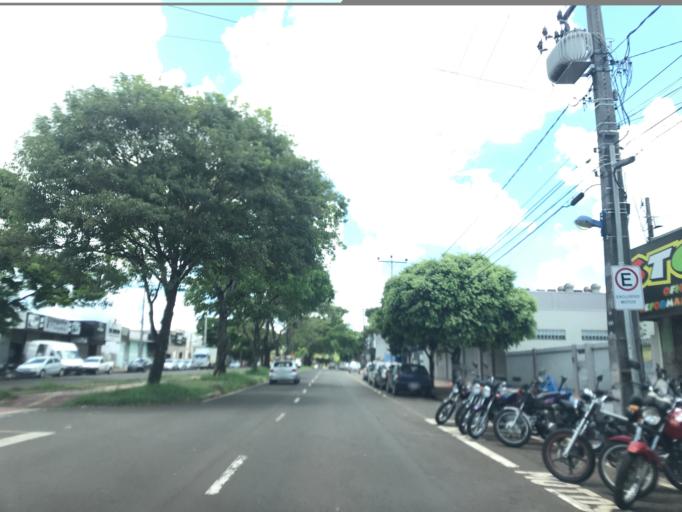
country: BR
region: Parana
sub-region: Maringa
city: Maringa
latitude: -23.3931
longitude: -51.9173
